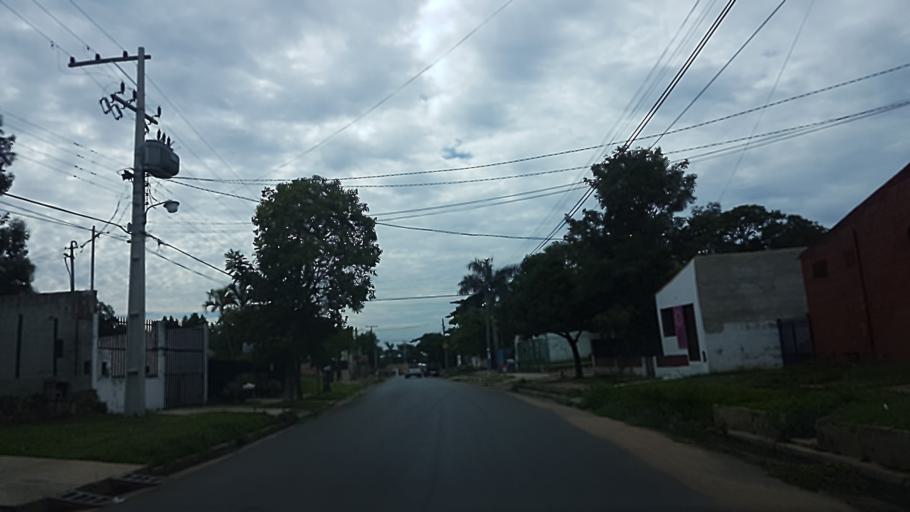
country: PY
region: Central
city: Colonia Mariano Roque Alonso
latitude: -25.2195
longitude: -57.5280
